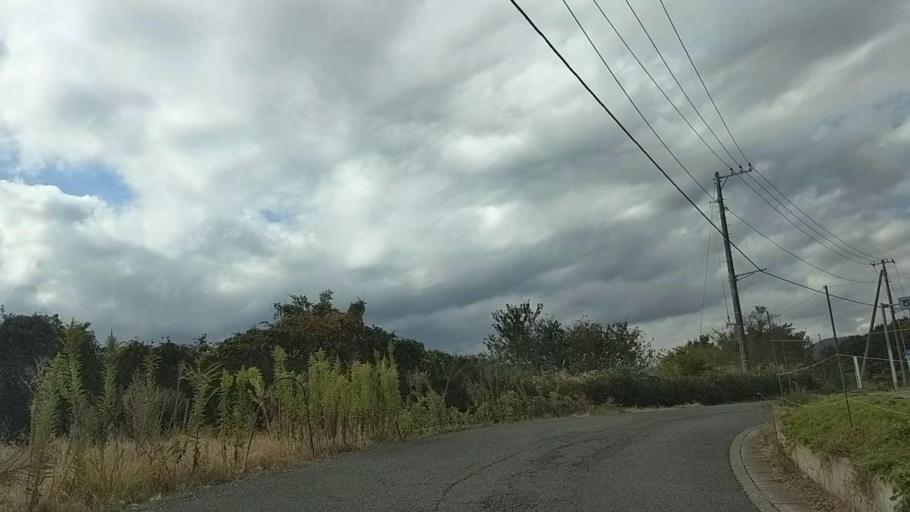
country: JP
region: Kanagawa
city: Hadano
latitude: 35.3517
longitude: 139.1736
